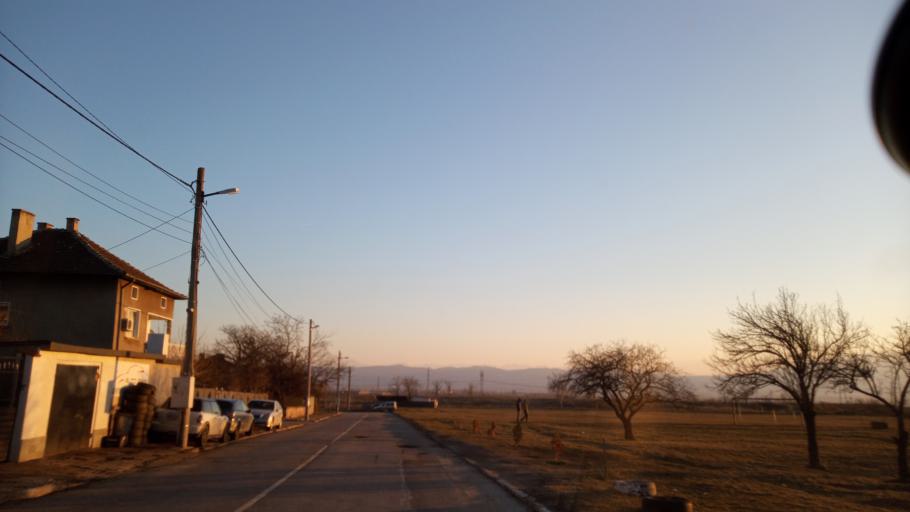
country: BG
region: Sofia-Capital
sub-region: Stolichna Obshtina
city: Bukhovo
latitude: 42.7812
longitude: 23.5179
